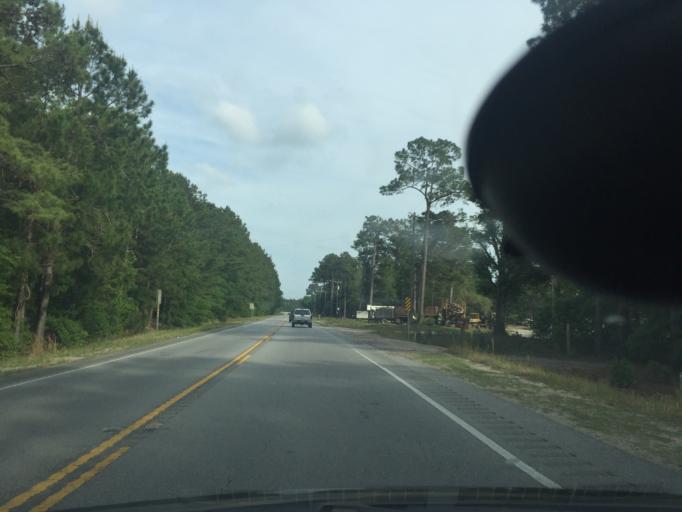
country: US
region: Georgia
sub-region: Chatham County
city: Bloomingdale
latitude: 32.0765
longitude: -81.3675
